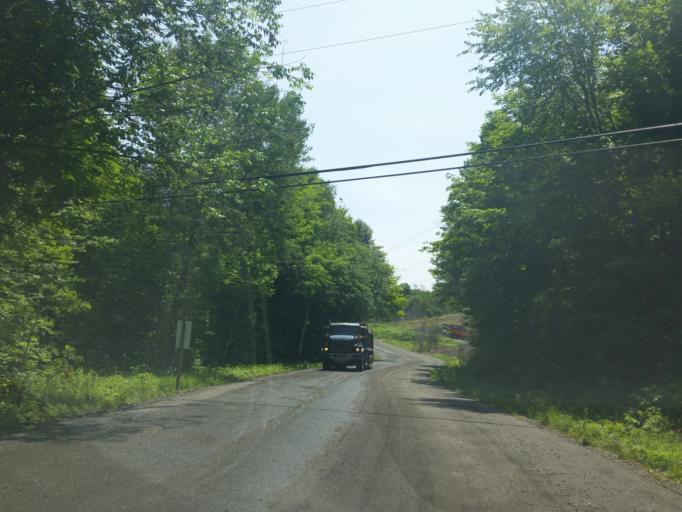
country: CA
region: Ontario
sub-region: Parry Sound District
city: Parry Sound
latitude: 45.4334
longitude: -80.0142
